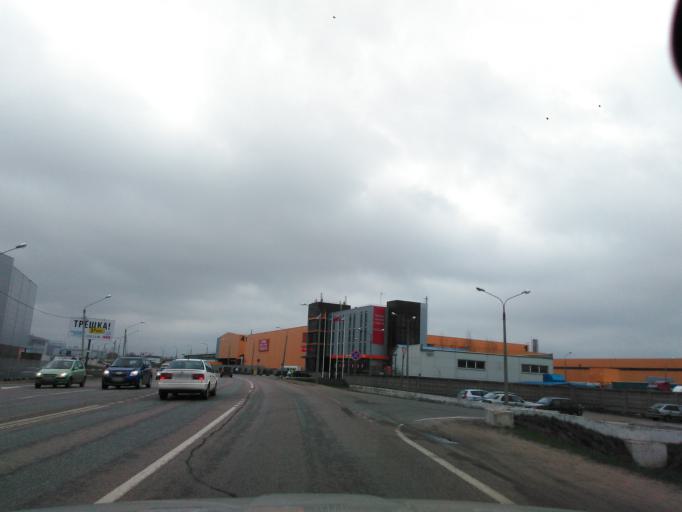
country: RU
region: Moskovskaya
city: Pavlovskaya Sloboda
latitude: 55.8152
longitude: 37.1142
